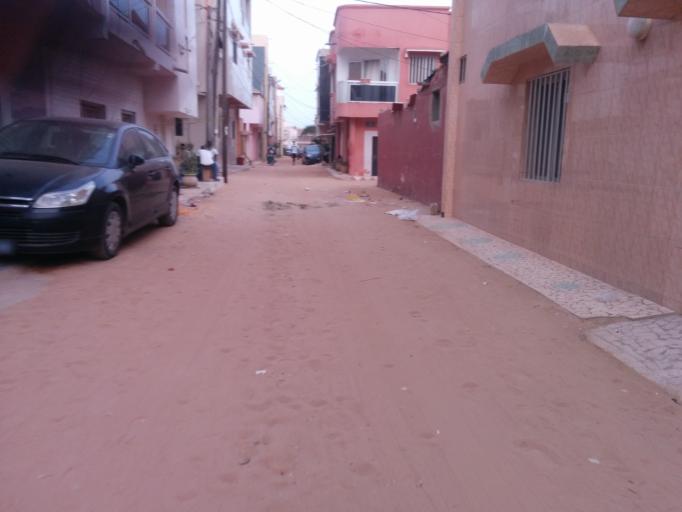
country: SN
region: Dakar
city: Grand Dakar
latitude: 14.7626
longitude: -17.4519
